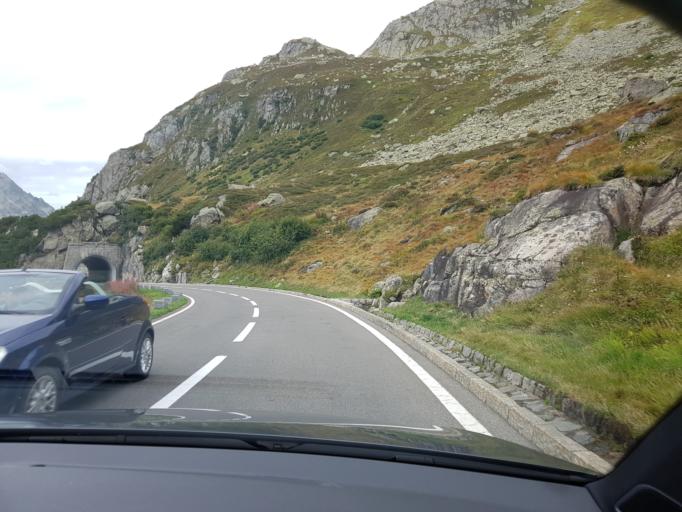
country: CH
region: Obwalden
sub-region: Obwalden
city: Engelberg
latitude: 46.7346
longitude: 8.4259
